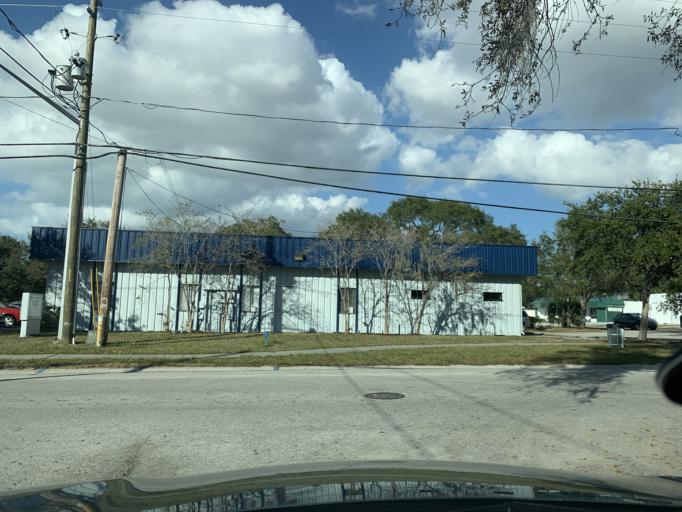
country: US
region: Florida
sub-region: Pinellas County
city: Belleair
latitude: 27.9425
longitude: -82.7920
